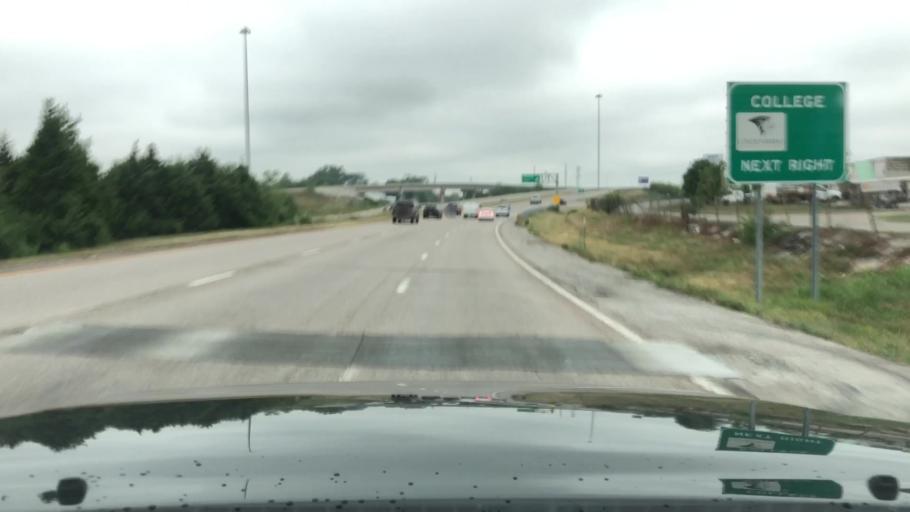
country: US
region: Missouri
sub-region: Saint Charles County
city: Wentzville
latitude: 38.8089
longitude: -90.8390
